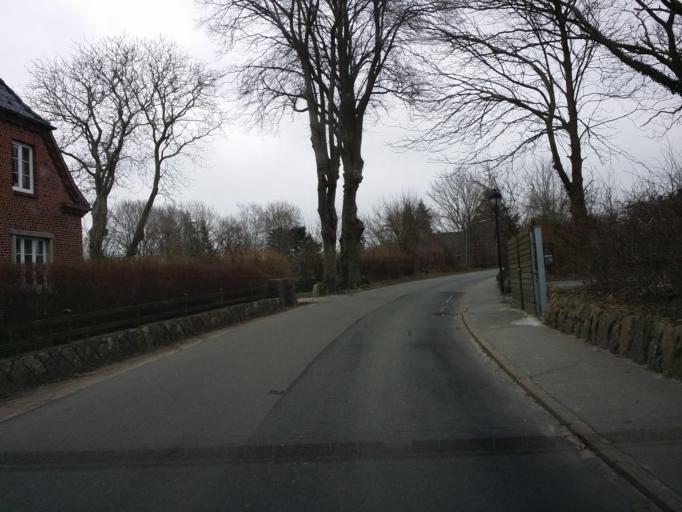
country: DE
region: Schleswig-Holstein
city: Bovenau
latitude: 54.3319
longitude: 9.8318
